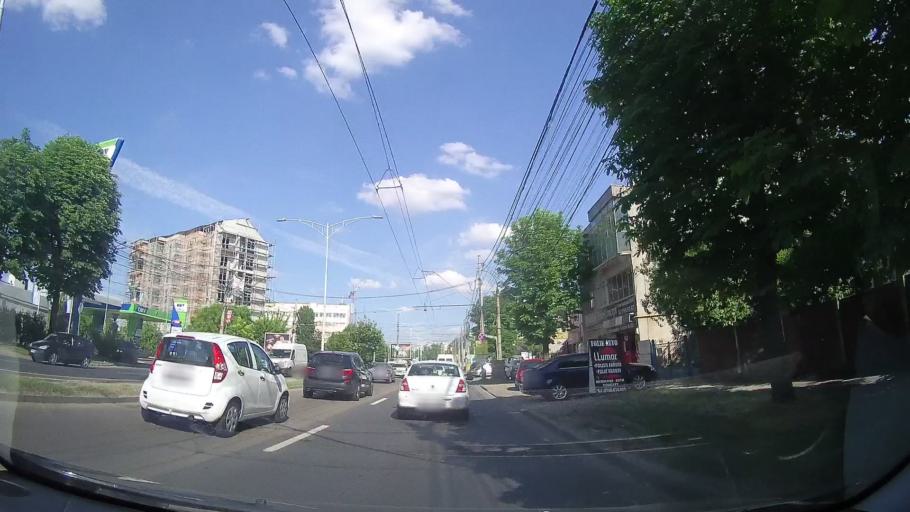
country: RO
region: Ilfov
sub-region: Comuna Chiajna
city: Rosu
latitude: 44.4339
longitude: 25.9948
